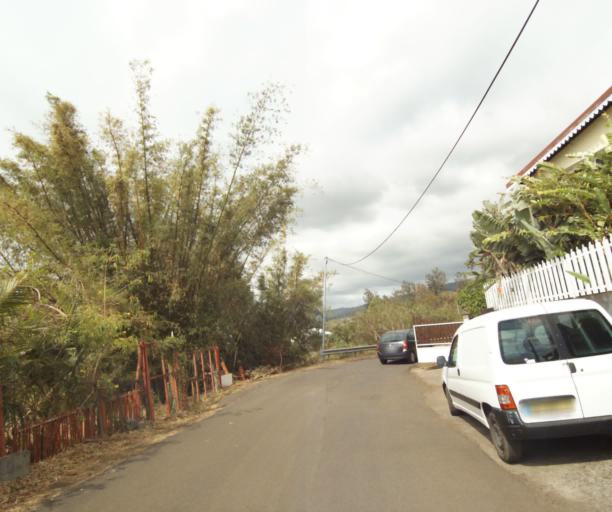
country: RE
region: Reunion
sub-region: Reunion
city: Saint-Paul
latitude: -21.0316
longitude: 55.2945
